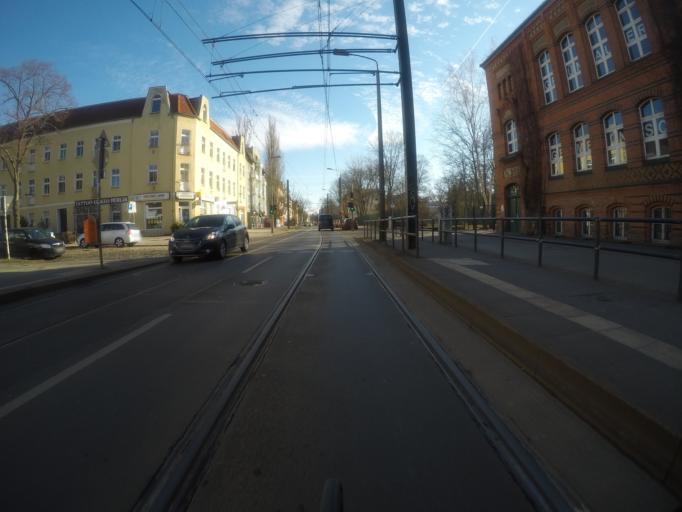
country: DE
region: Berlin
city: Grunau
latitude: 52.4205
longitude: 13.5778
